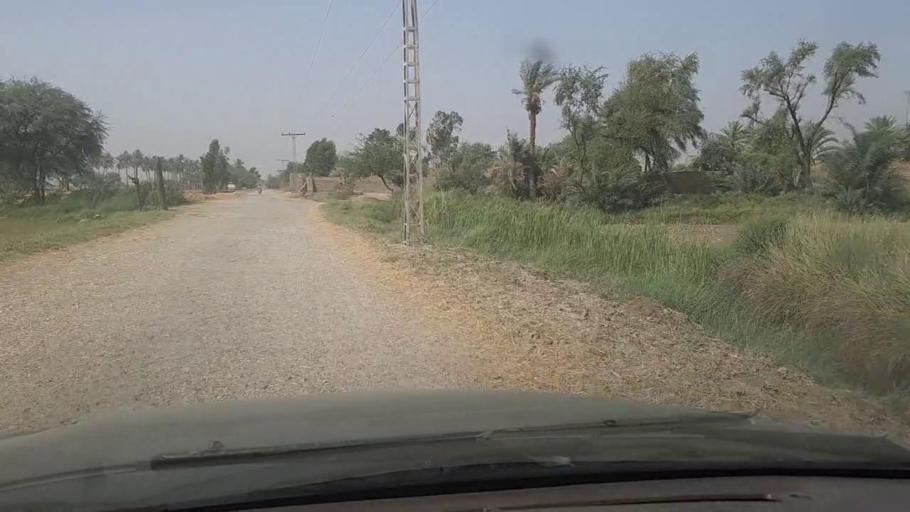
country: PK
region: Sindh
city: Garhi Yasin
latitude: 27.8740
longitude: 68.5611
